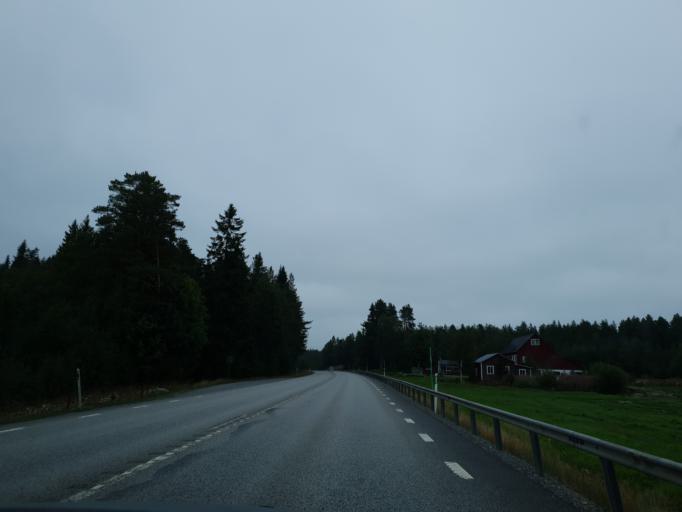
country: SE
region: Vaesterbotten
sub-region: Robertsfors Kommun
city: Robertsfors
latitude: 64.2528
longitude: 21.0425
